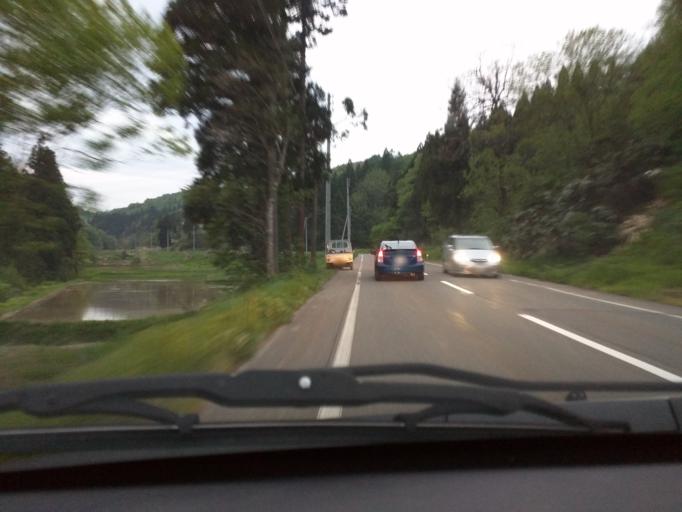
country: JP
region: Niigata
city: Ojiya
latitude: 37.3198
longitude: 138.6975
